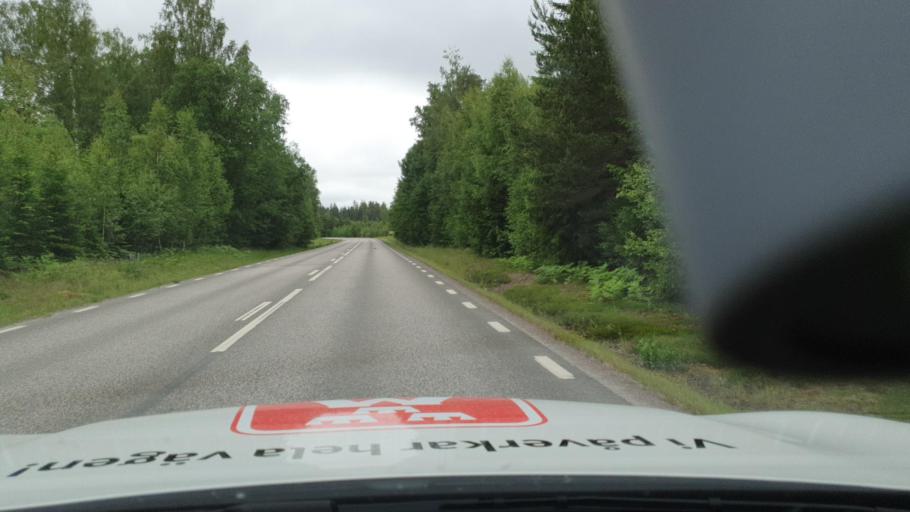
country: SE
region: Vaestra Goetaland
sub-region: Tibro Kommun
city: Tibro
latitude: 58.3818
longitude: 14.2025
